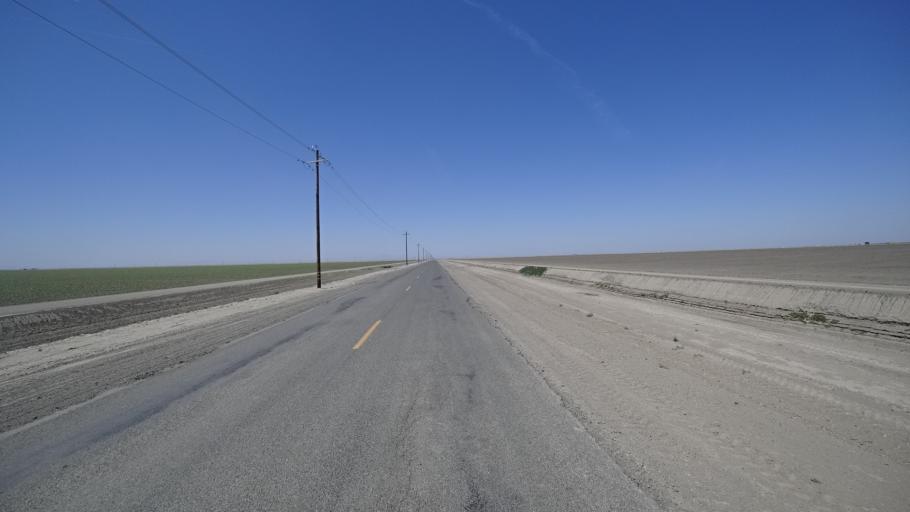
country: US
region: California
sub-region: Kings County
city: Corcoran
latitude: 36.0215
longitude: -119.6303
